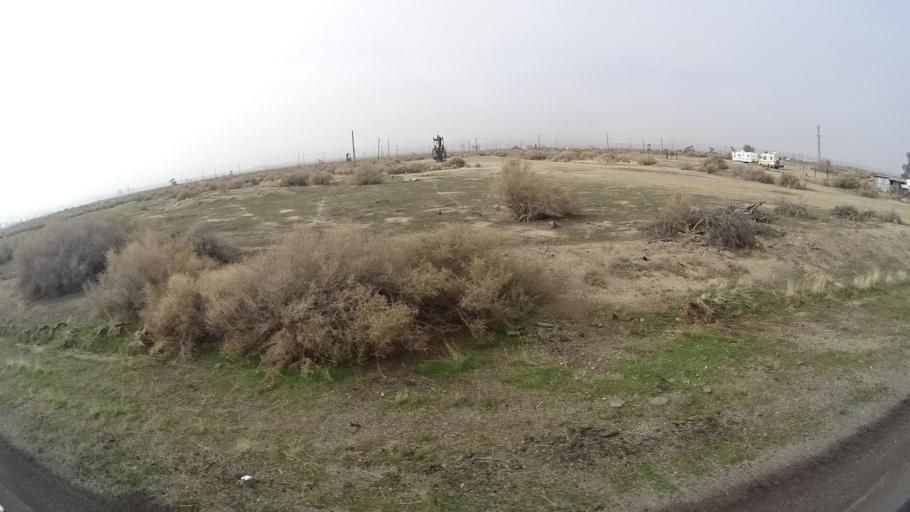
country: US
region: California
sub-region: Kern County
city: Maricopa
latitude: 35.0540
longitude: -119.3492
